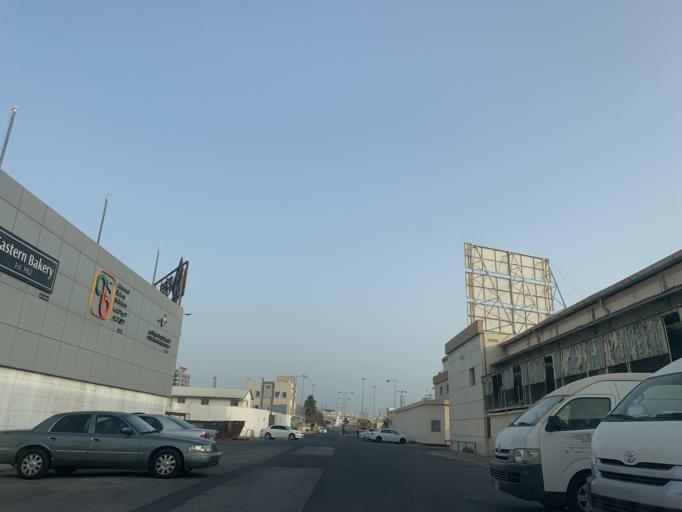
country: BH
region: Manama
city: Manama
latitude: 26.1994
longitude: 50.6042
